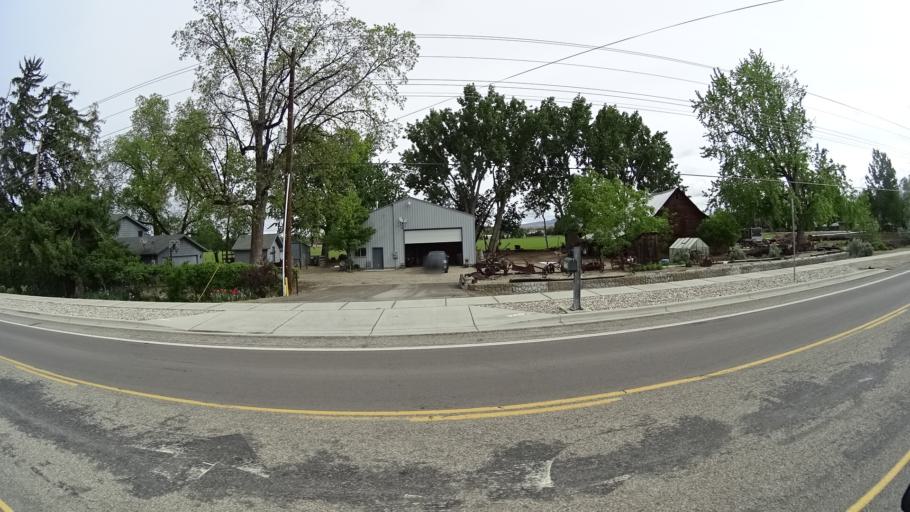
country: US
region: Idaho
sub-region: Ada County
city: Eagle
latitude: 43.6956
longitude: -116.3759
